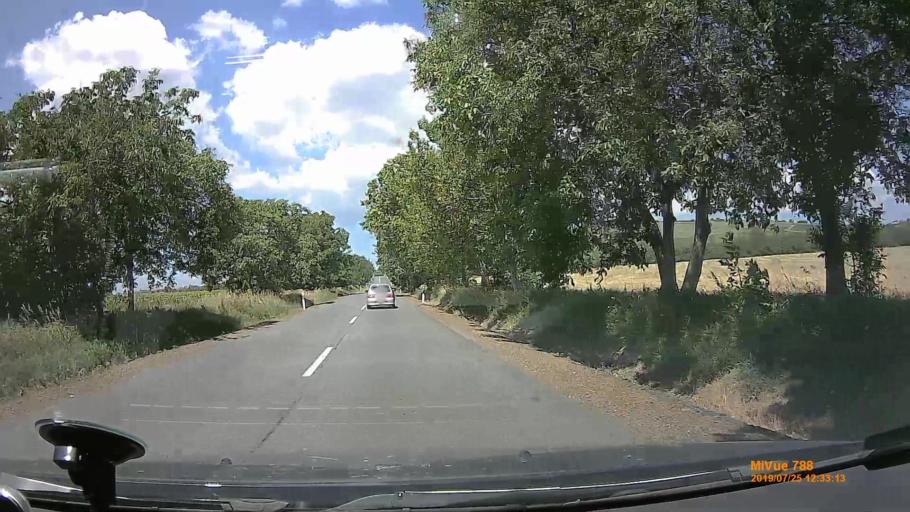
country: HU
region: Borsod-Abauj-Zemplen
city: Mezozombor
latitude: 48.1597
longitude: 21.3091
